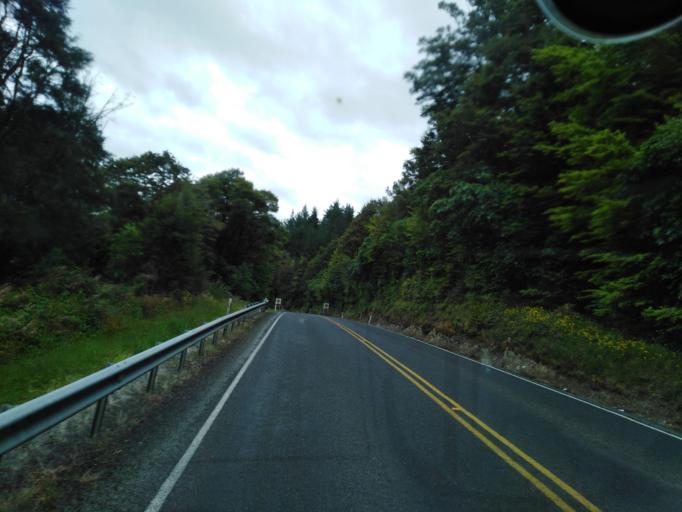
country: NZ
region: Tasman
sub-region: Tasman District
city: Wakefield
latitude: -41.7036
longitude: 172.5894
